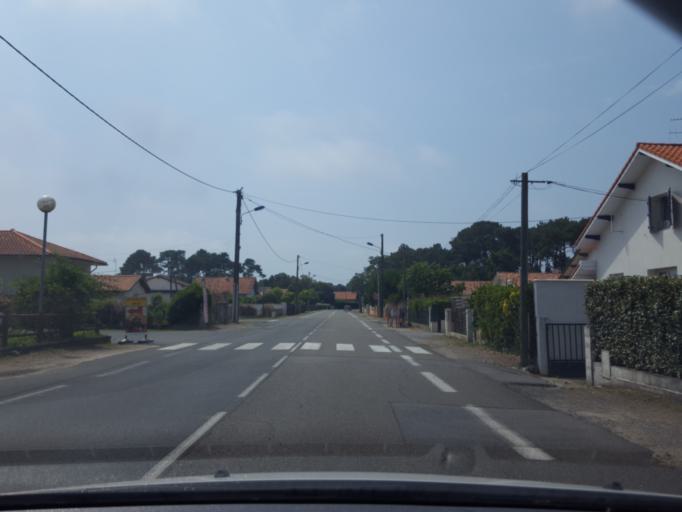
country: FR
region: Aquitaine
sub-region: Departement des Landes
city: Ondres
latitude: 43.5702
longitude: -1.4642
